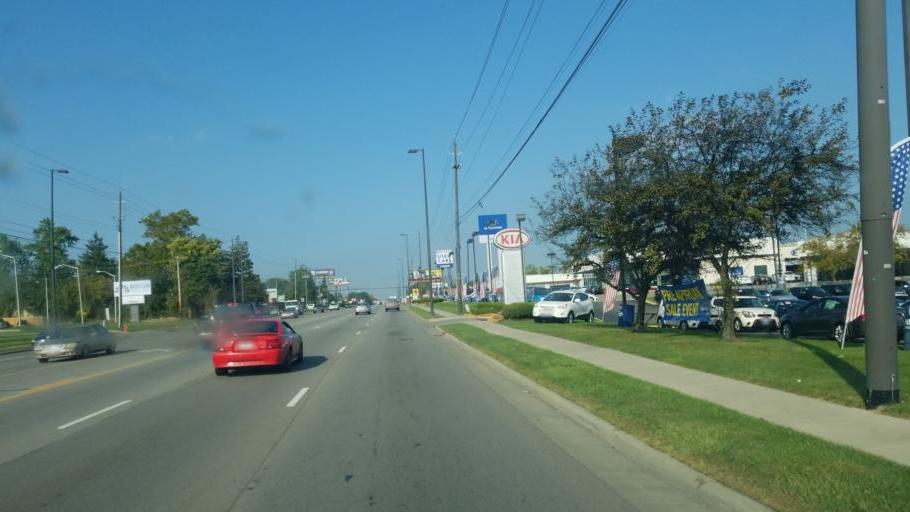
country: US
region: Ohio
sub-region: Franklin County
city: Minerva Park
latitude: 40.0591
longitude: -82.9410
